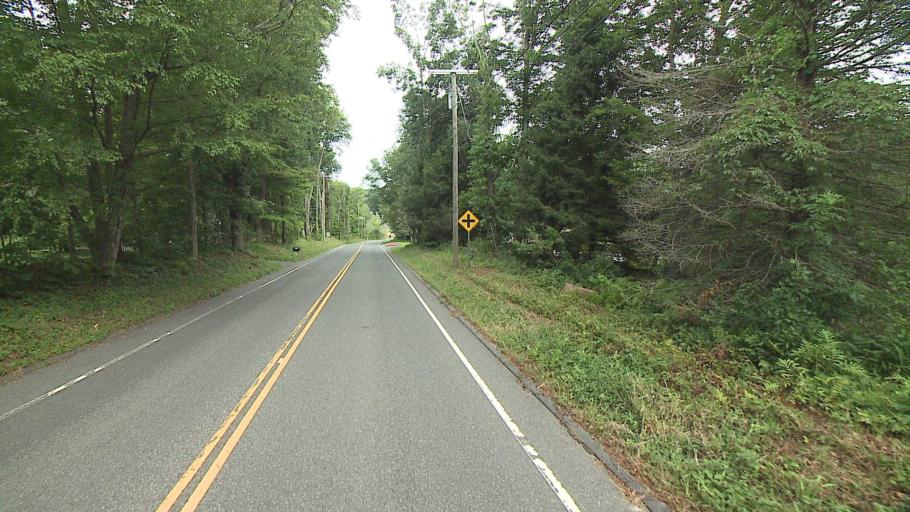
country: US
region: Connecticut
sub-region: Litchfield County
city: New Preston
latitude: 41.6172
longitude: -73.2932
